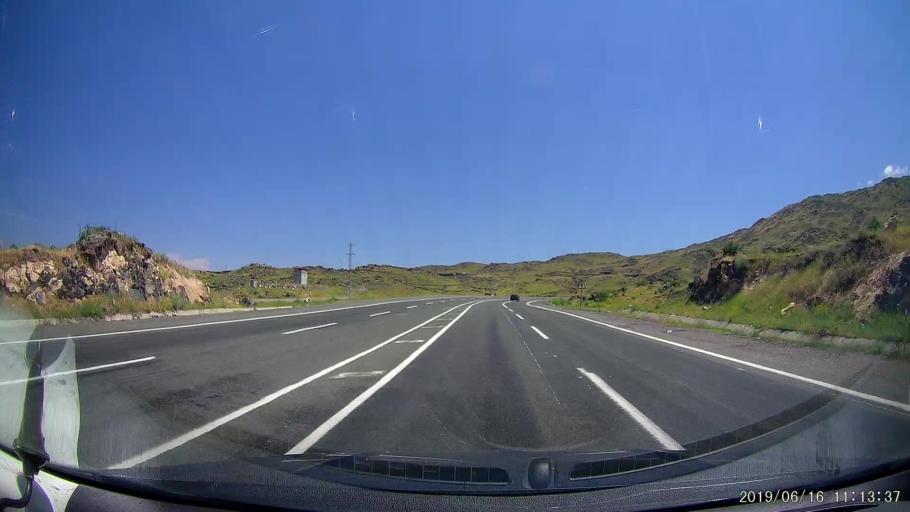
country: TR
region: Igdir
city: Igdir
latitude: 39.7854
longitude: 44.1409
